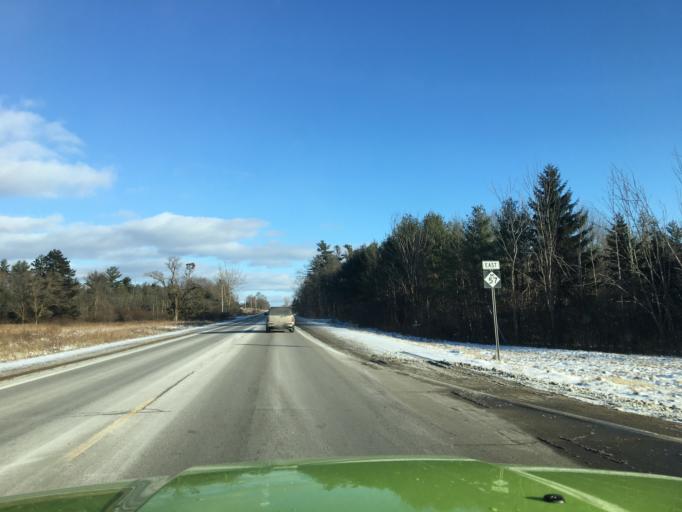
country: US
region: Michigan
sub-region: Kent County
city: Cedar Springs
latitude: 43.1755
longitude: -85.5204
